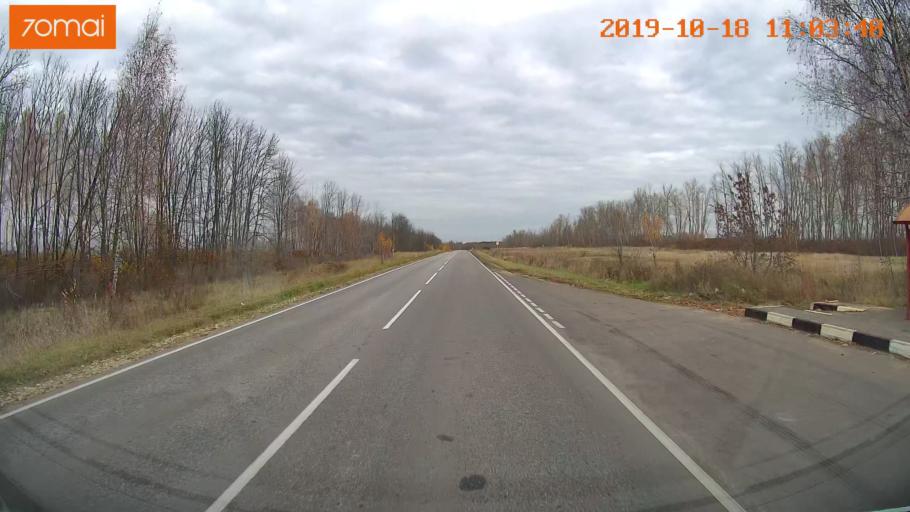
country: RU
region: Tula
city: Yepifan'
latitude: 53.8832
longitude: 38.5492
